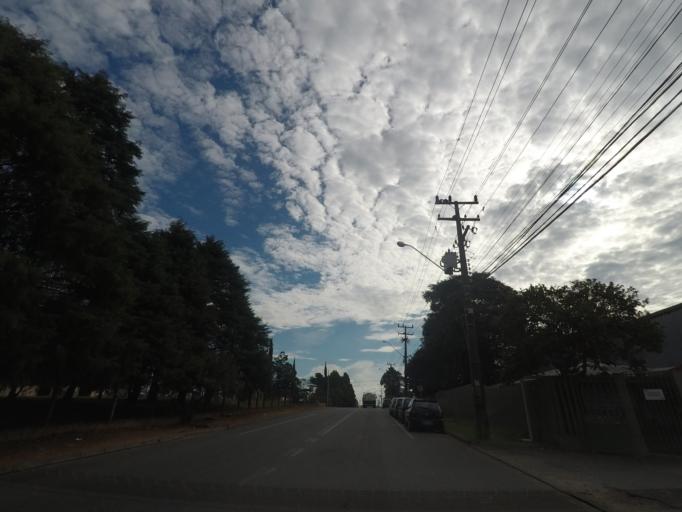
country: BR
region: Parana
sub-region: Araucaria
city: Araucaria
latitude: -25.6414
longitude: -49.3046
